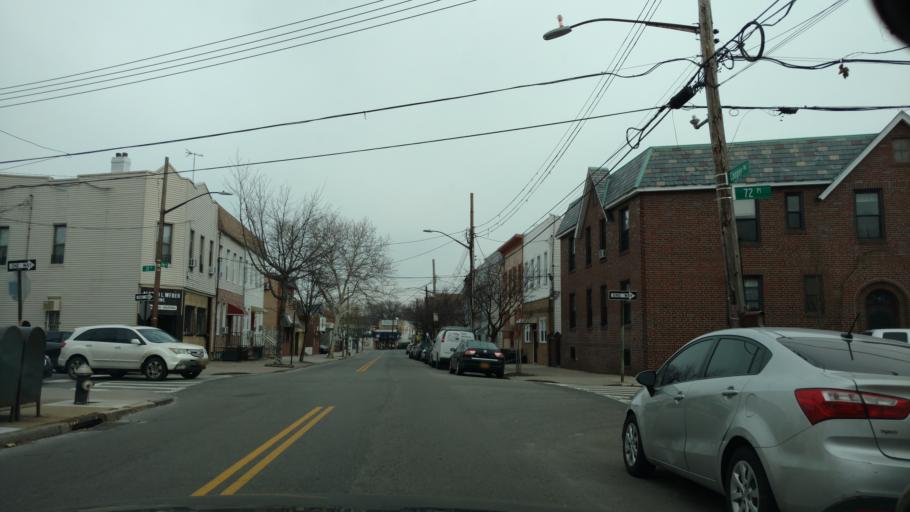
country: US
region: New York
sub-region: Kings County
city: East New York
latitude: 40.7035
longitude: -73.8781
